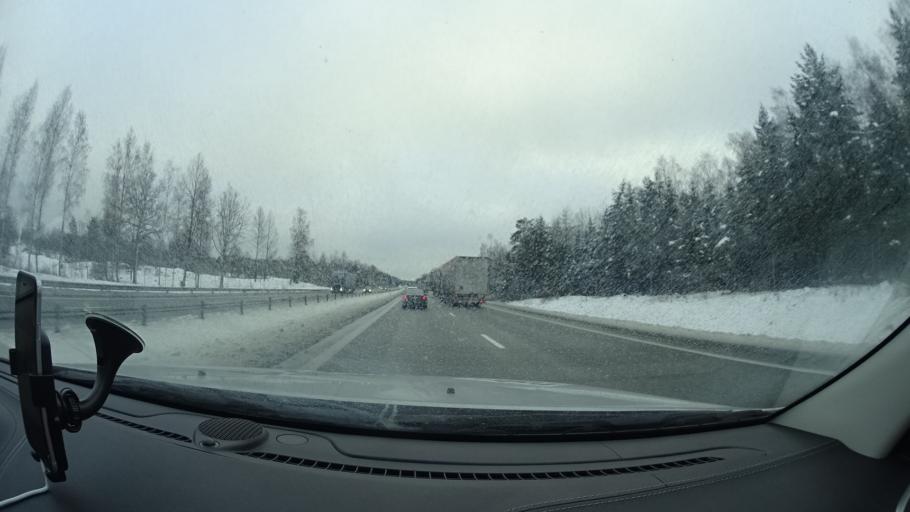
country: SE
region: Joenkoeping
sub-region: Jonkopings Kommun
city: Asa
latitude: 58.0779
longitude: 14.5365
